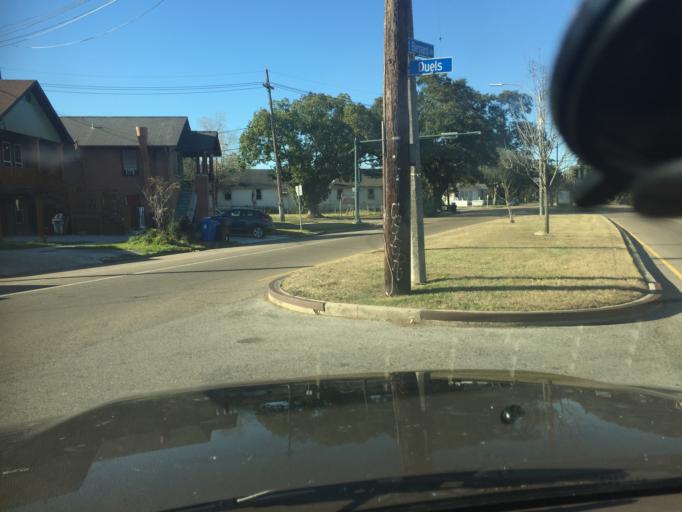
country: US
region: Louisiana
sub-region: Orleans Parish
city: New Orleans
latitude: 29.9849
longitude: -90.0726
